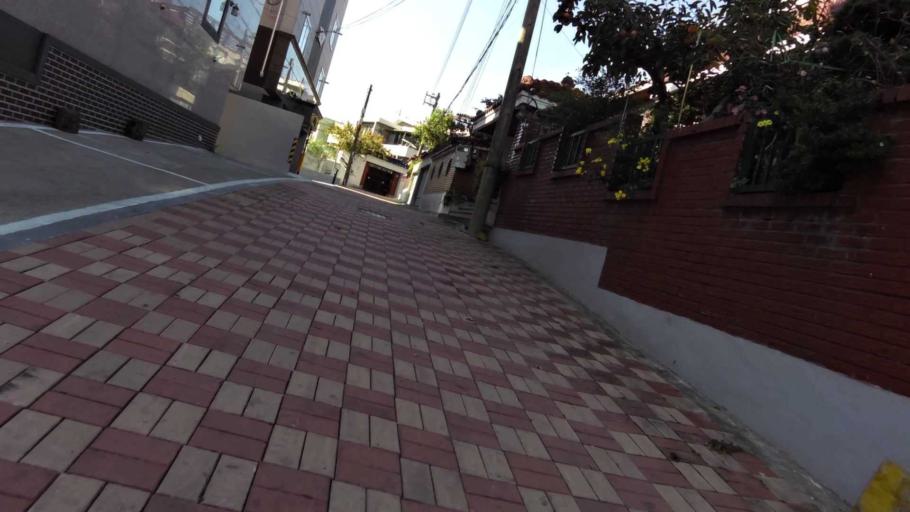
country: KR
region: Daegu
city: Daegu
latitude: 35.8607
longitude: 128.6458
